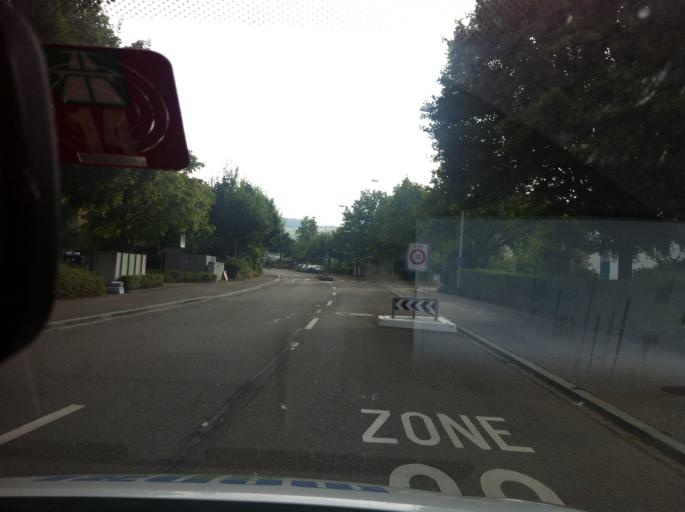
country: CH
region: Zurich
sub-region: Bezirk Buelach
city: Buelach / Seematt
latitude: 47.5148
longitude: 8.5430
